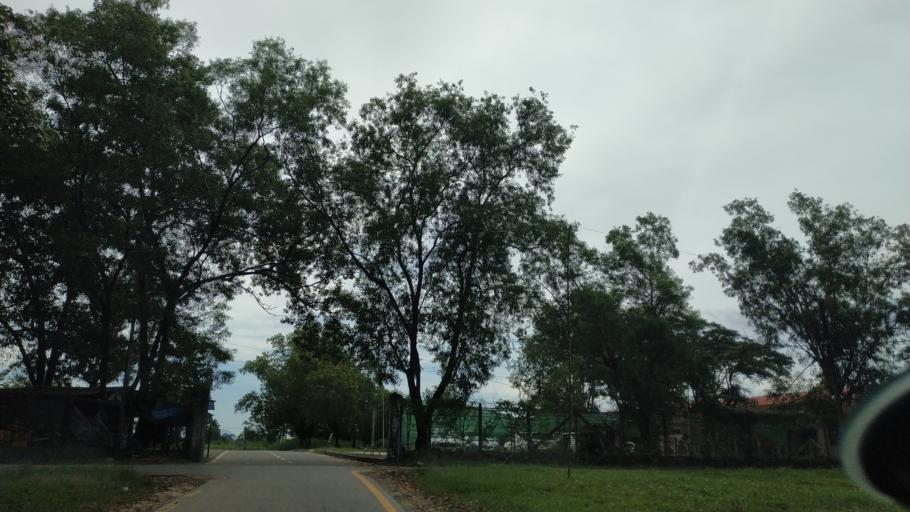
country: MM
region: Tanintharyi
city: Dawei
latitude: 14.0993
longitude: 98.2027
